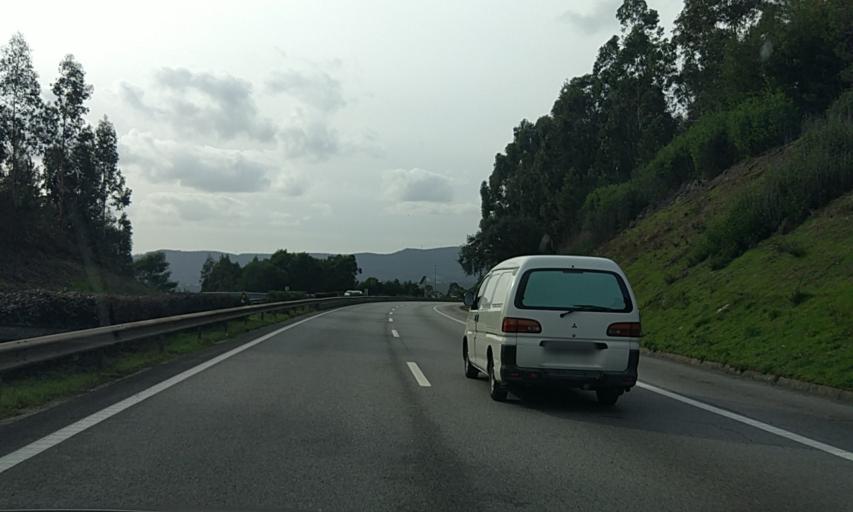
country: PT
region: Porto
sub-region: Paredes
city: Recarei
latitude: 41.1663
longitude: -8.3939
